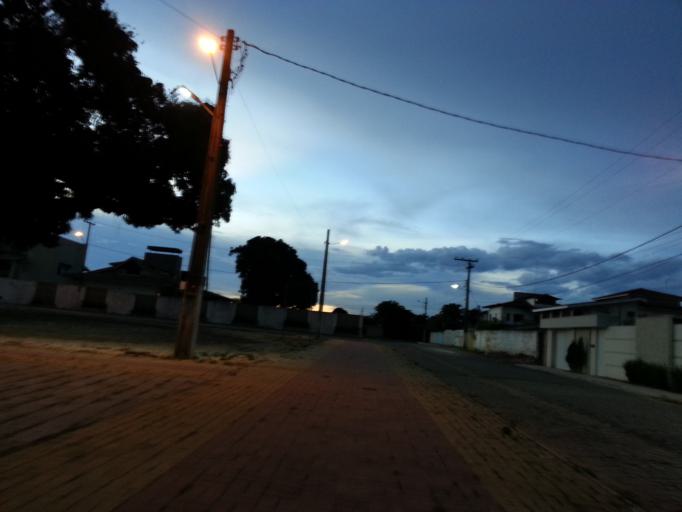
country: BR
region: Bahia
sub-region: Cruz Das Almas
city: Cruz das Almas
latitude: -12.6763
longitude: -39.1079
